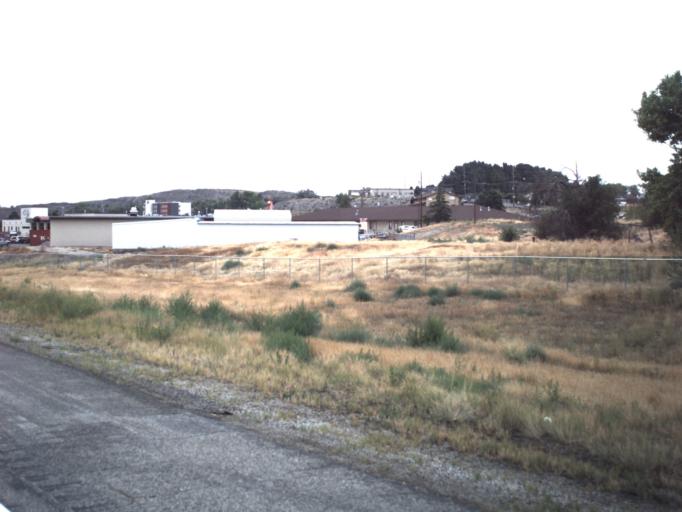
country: US
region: Utah
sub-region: Carbon County
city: Carbonville
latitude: 39.6079
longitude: -110.8333
